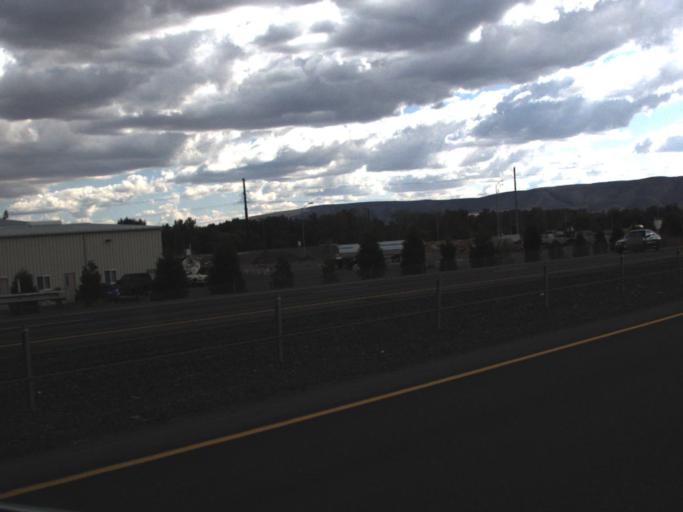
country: US
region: Washington
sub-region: Yakima County
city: Union Gap
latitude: 46.5797
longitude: -120.4720
